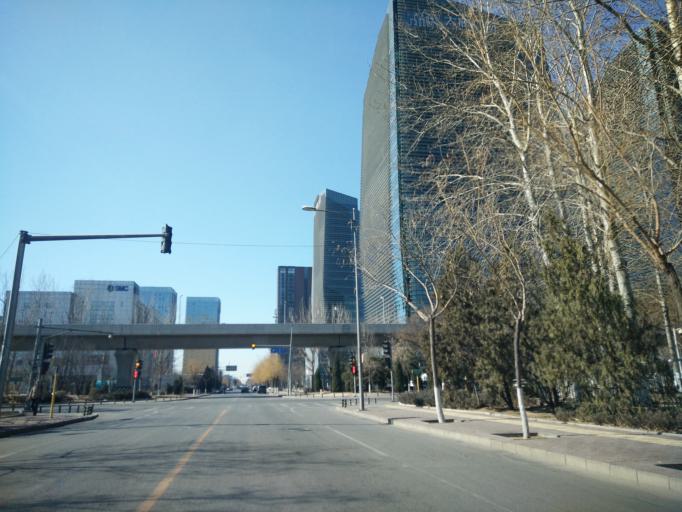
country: CN
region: Beijing
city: Jiugong
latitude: 39.7903
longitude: 116.5099
